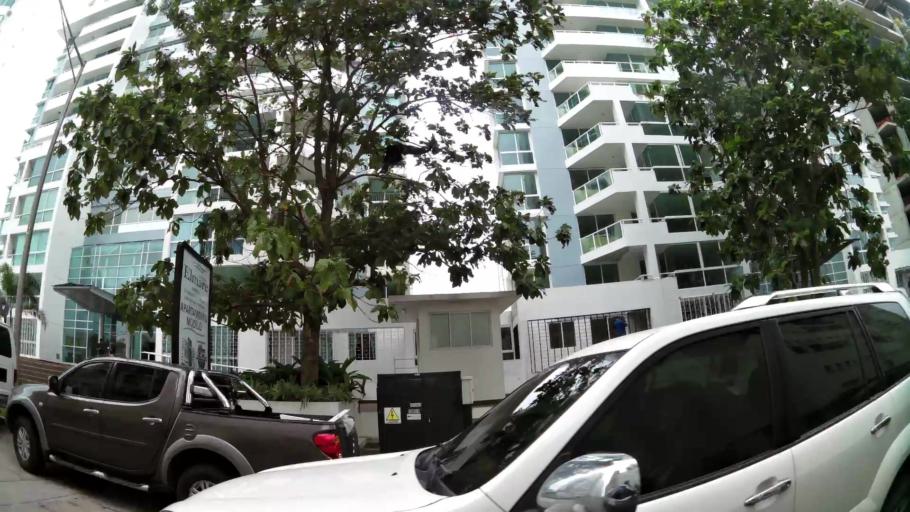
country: PA
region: Panama
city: Panama
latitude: 8.9948
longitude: -79.5323
